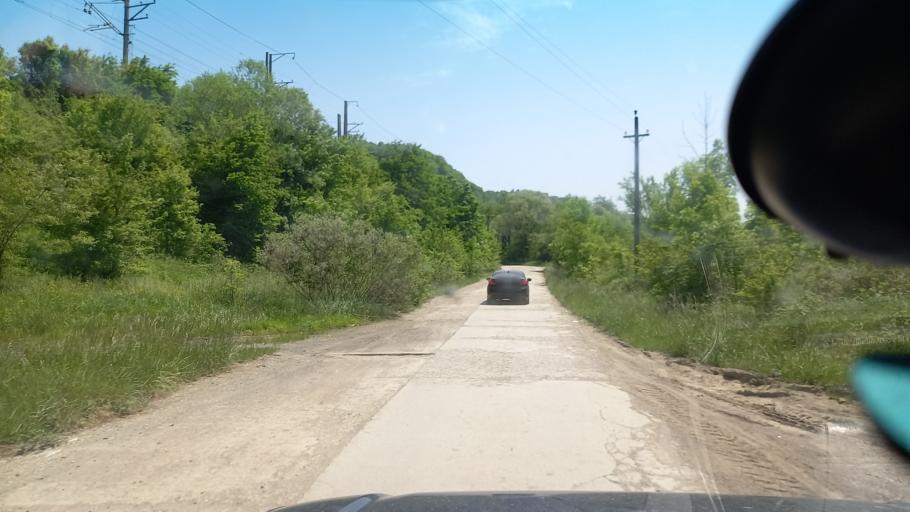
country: RU
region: Krasnodarskiy
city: Tuapse
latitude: 44.2414
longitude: 39.2405
